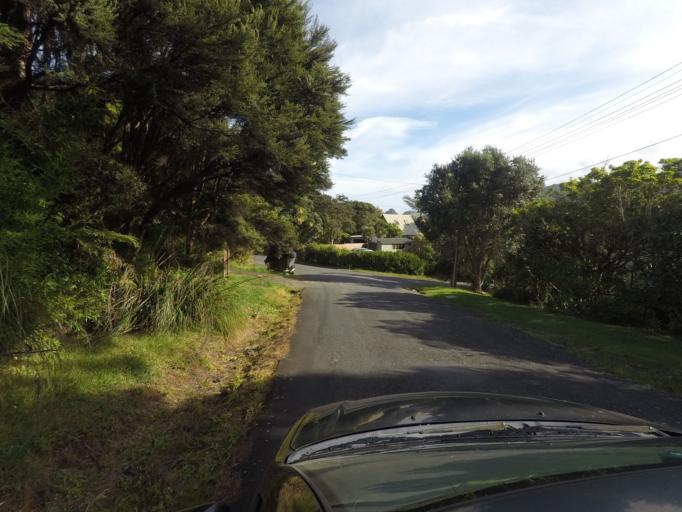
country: NZ
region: Auckland
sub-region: Auckland
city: Titirangi
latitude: -36.9974
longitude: 174.5760
